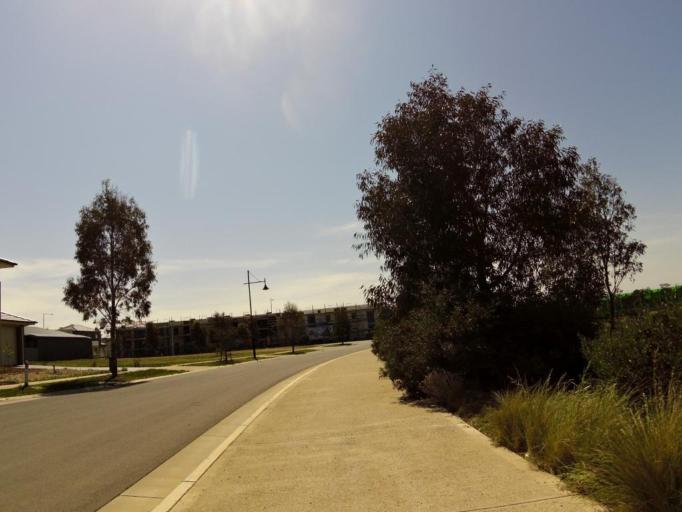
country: AU
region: Victoria
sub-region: Wyndham
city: Hoppers Crossing
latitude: -37.8788
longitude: 144.7220
